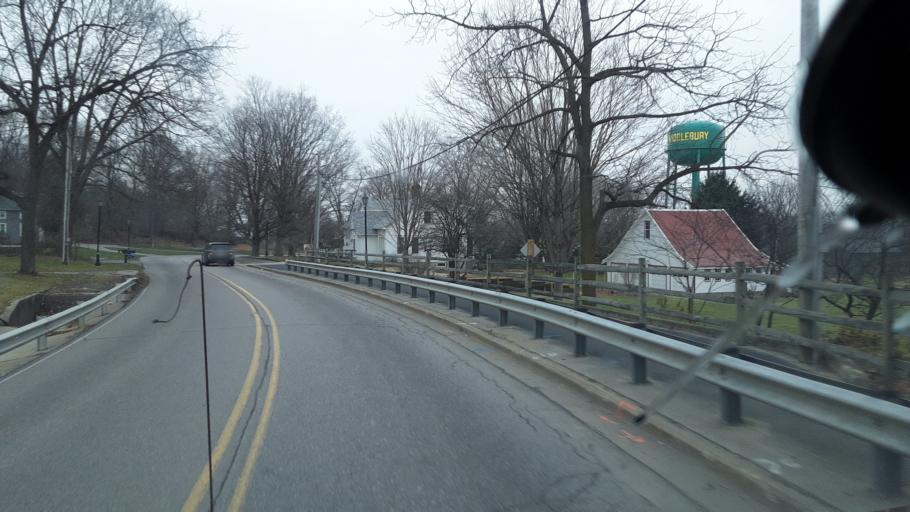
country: US
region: Indiana
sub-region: Elkhart County
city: Middlebury
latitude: 41.6712
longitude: -85.7109
